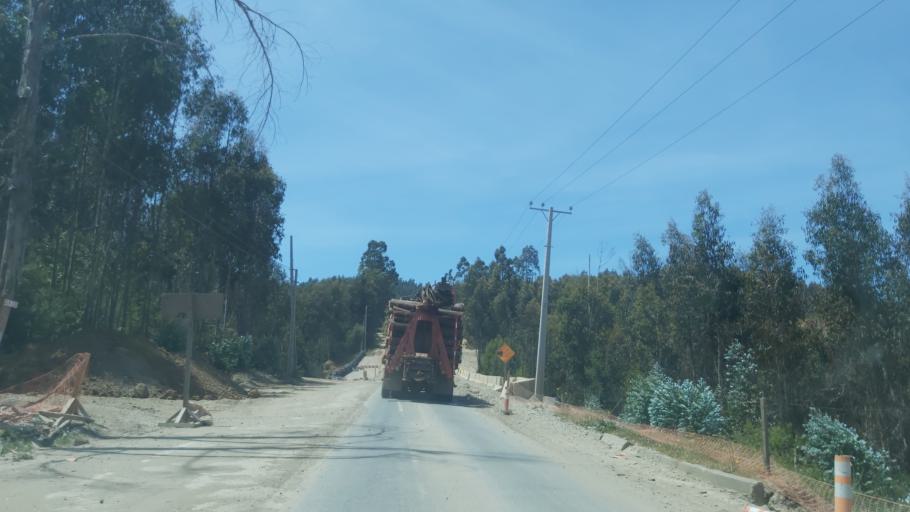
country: CL
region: Maule
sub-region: Provincia de Talca
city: Constitucion
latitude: -35.4457
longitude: -72.4666
